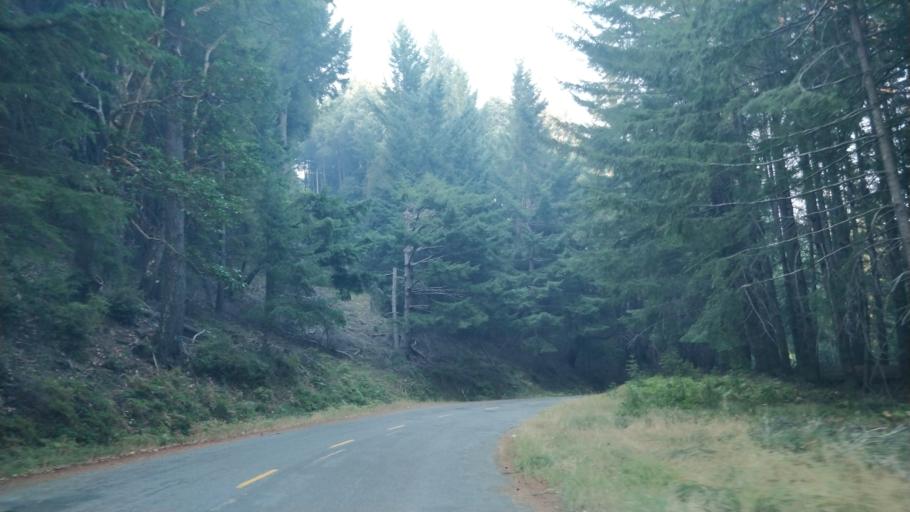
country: US
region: California
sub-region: Humboldt County
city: Rio Dell
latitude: 40.2993
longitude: -124.0569
